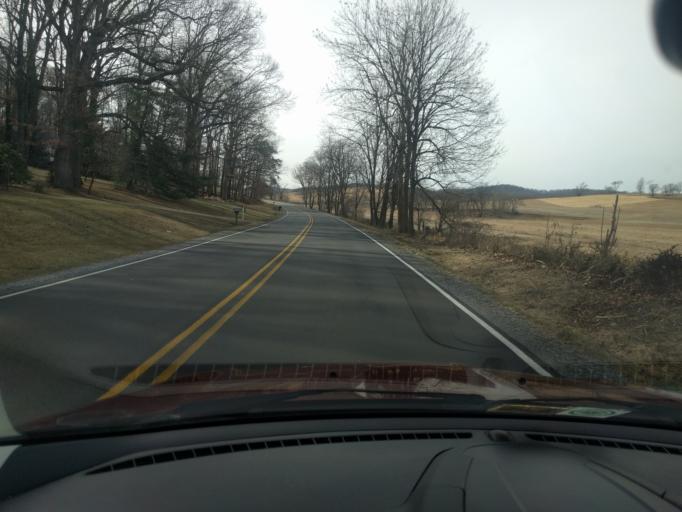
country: US
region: Virginia
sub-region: Augusta County
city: Stuarts Draft
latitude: 38.0425
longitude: -79.1022
